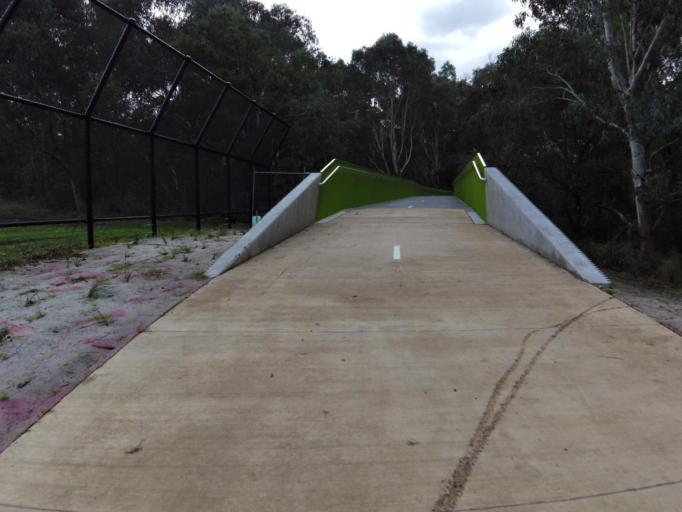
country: AU
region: Victoria
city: Alphington
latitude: -37.7826
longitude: 145.0376
